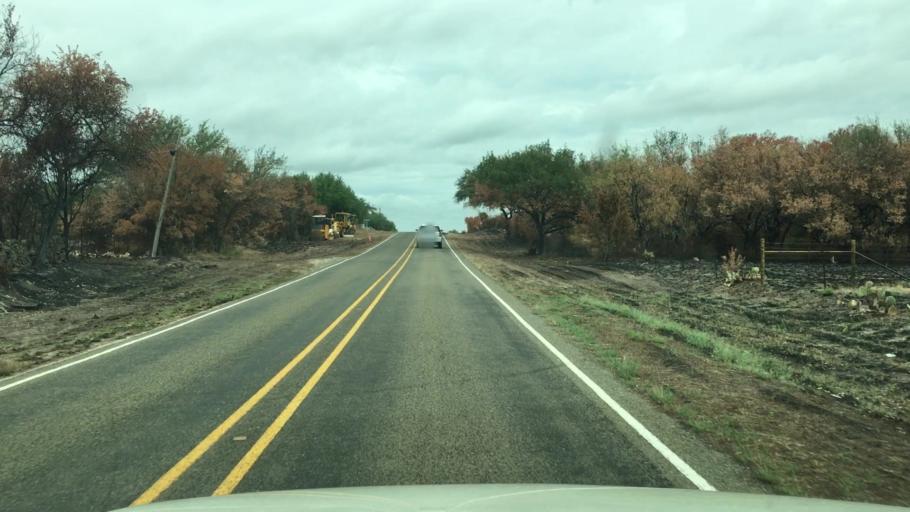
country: US
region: Texas
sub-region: Llano County
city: Horseshoe Bay
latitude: 30.4814
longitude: -98.4242
